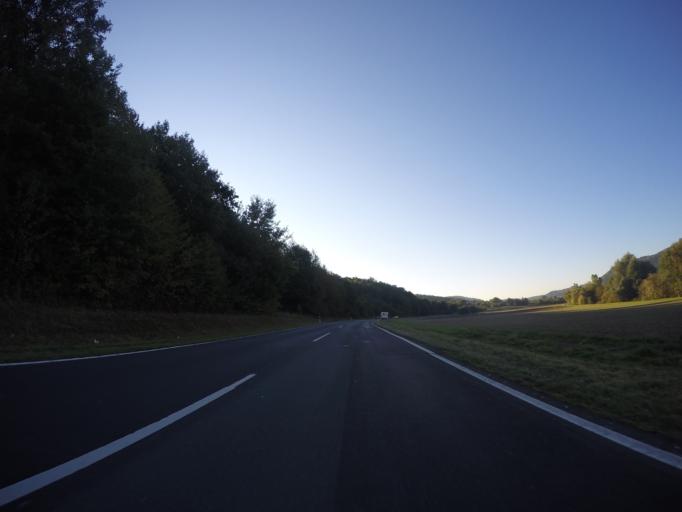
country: DE
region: Bavaria
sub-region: Regierungsbezirk Unterfranken
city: Kreuzwertheim
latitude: 49.7829
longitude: 9.5137
